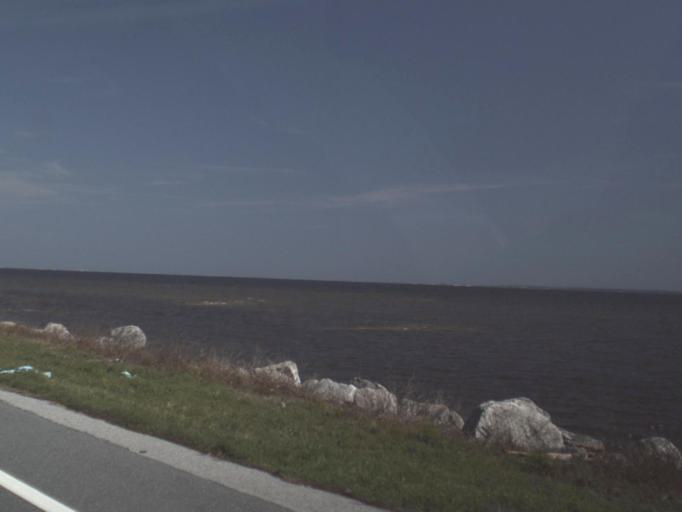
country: US
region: Florida
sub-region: Franklin County
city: Eastpoint
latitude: 29.7687
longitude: -84.8004
